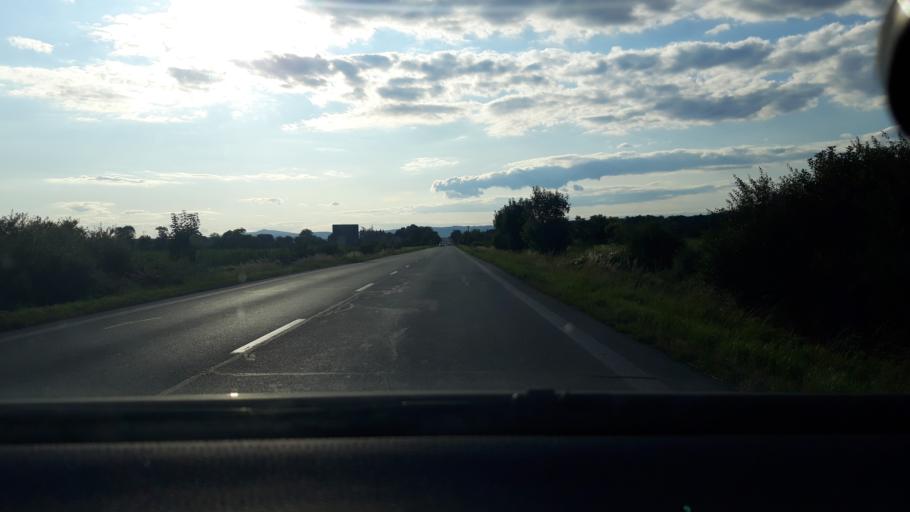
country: SK
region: Banskobystricky
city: Lucenec
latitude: 48.3032
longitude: 19.7290
